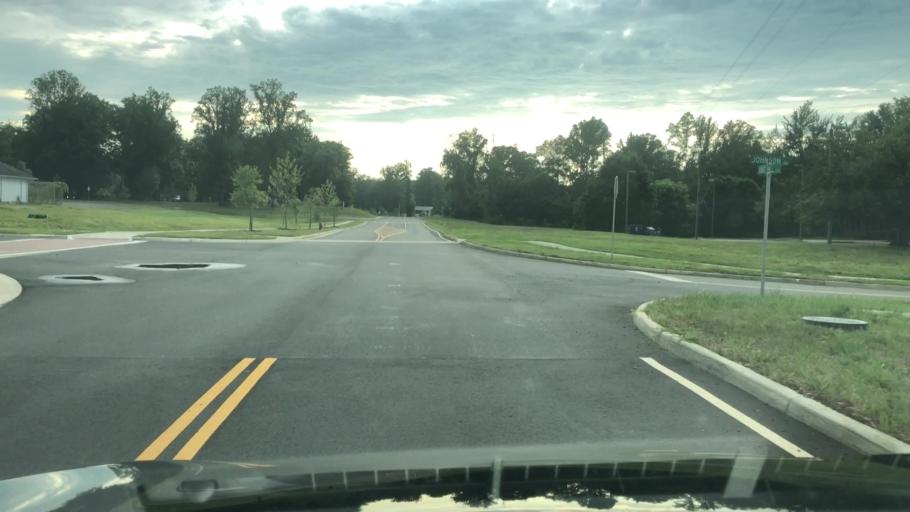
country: US
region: Virginia
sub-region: Fauquier County
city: New Baltimore
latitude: 38.7453
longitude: -77.6812
